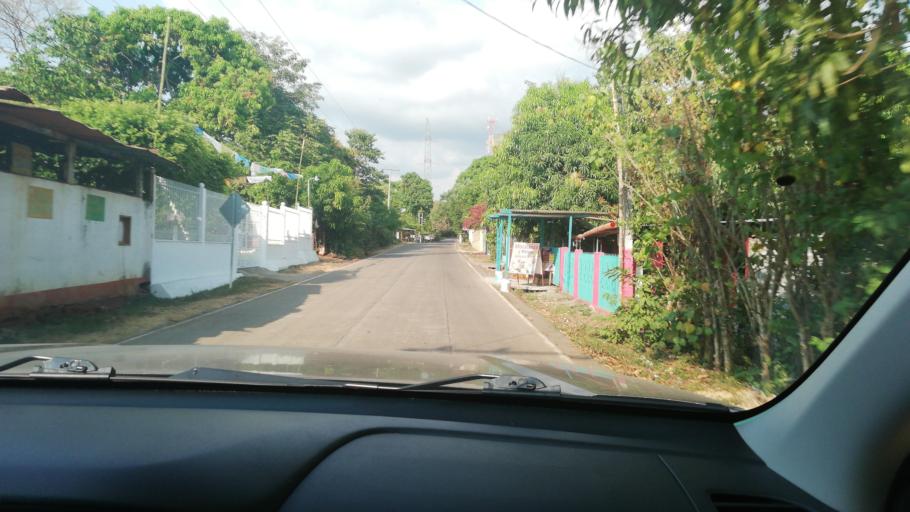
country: GT
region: Quetzaltenango
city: Genova
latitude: 14.5631
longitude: -91.8547
